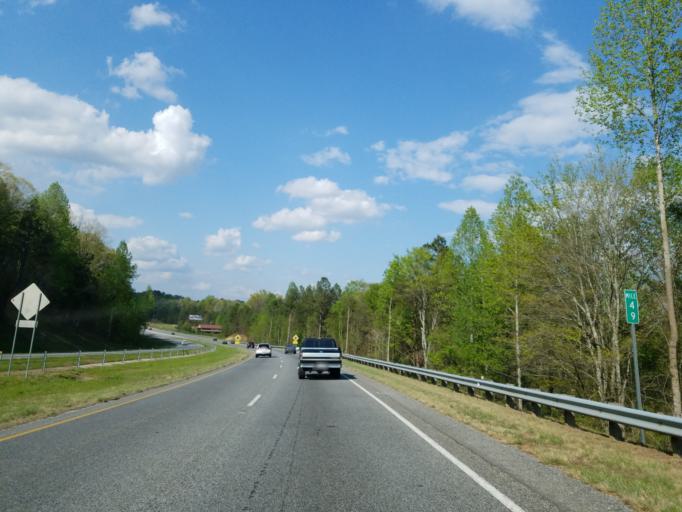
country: US
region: Georgia
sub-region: Lumpkin County
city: Dahlonega
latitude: 34.4100
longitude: -83.9951
